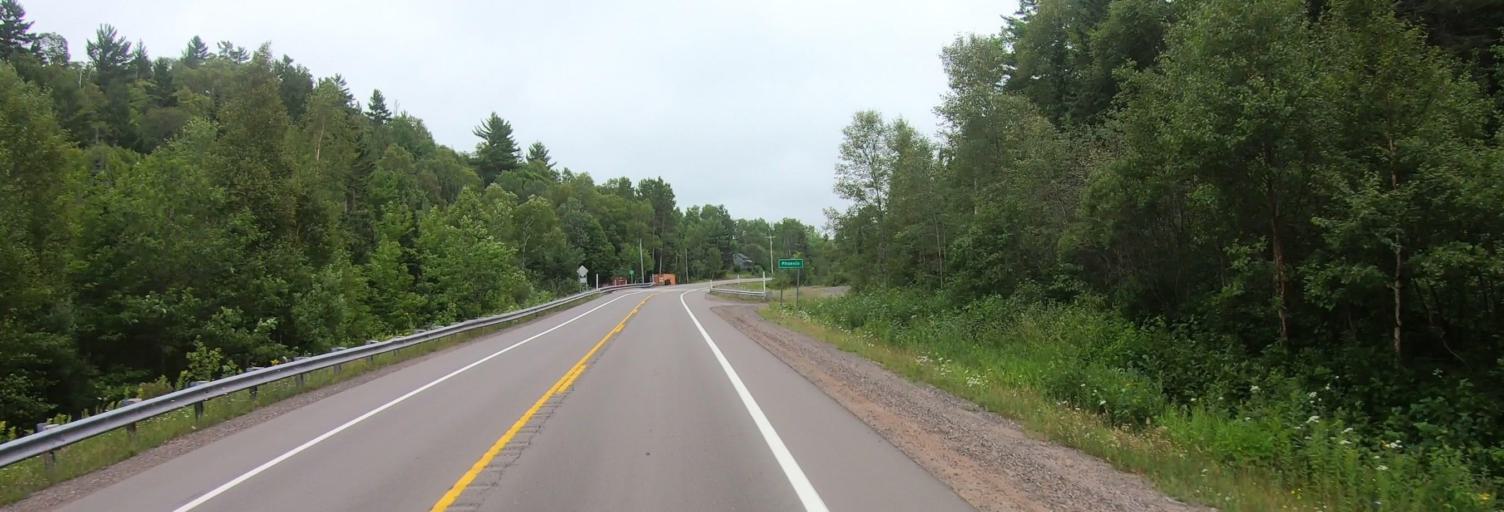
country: US
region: Michigan
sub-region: Keweenaw County
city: Eagle River
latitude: 47.3941
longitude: -88.2772
